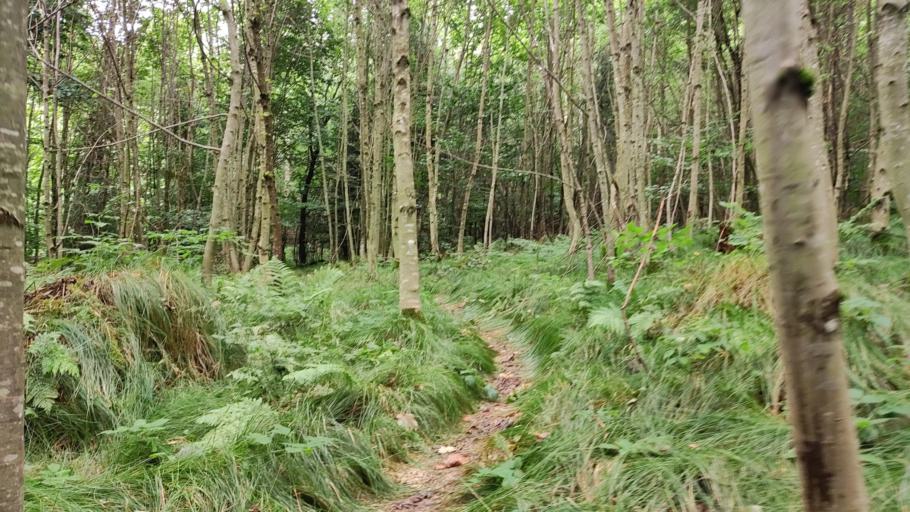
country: DE
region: Bavaria
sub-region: Swabia
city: Jettingen-Scheppach
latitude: 48.3784
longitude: 10.4023
